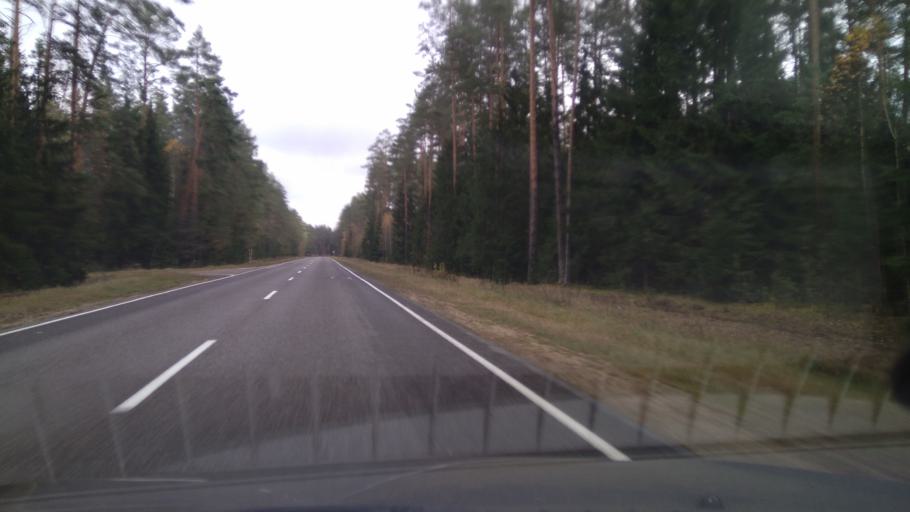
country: BY
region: Minsk
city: Urechcha
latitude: 53.2154
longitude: 27.8312
